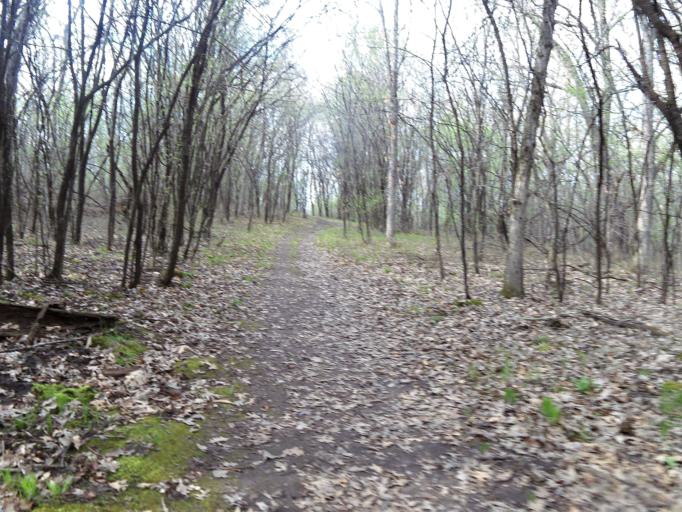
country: US
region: Wisconsin
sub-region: Saint Croix County
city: North Hudson
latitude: 45.0155
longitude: -92.6857
